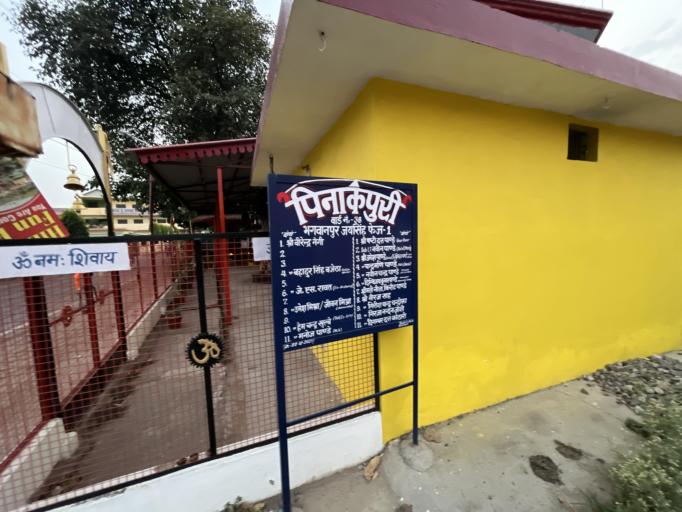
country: IN
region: Uttarakhand
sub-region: Naini Tal
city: Haldwani
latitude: 29.2263
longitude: 79.4841
